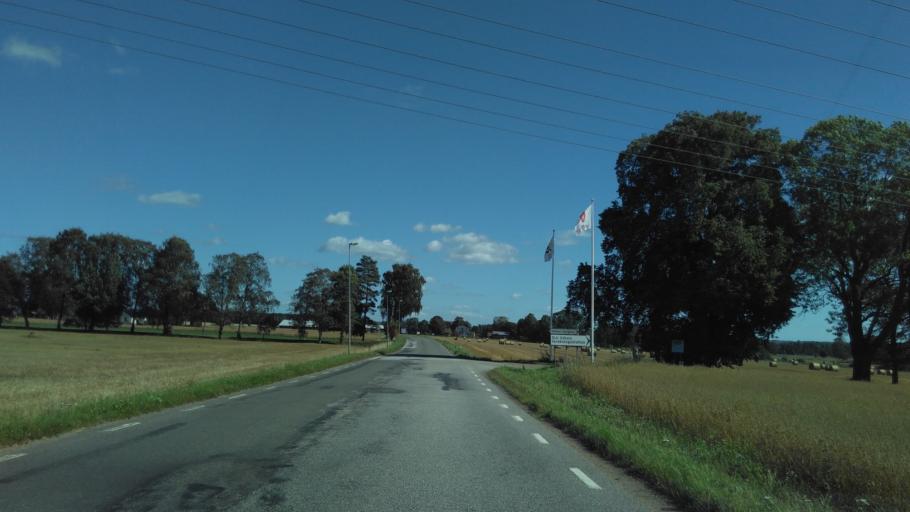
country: SE
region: Vaestra Goetaland
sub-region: Skara Kommun
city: Skara
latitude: 58.3842
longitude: 13.4736
